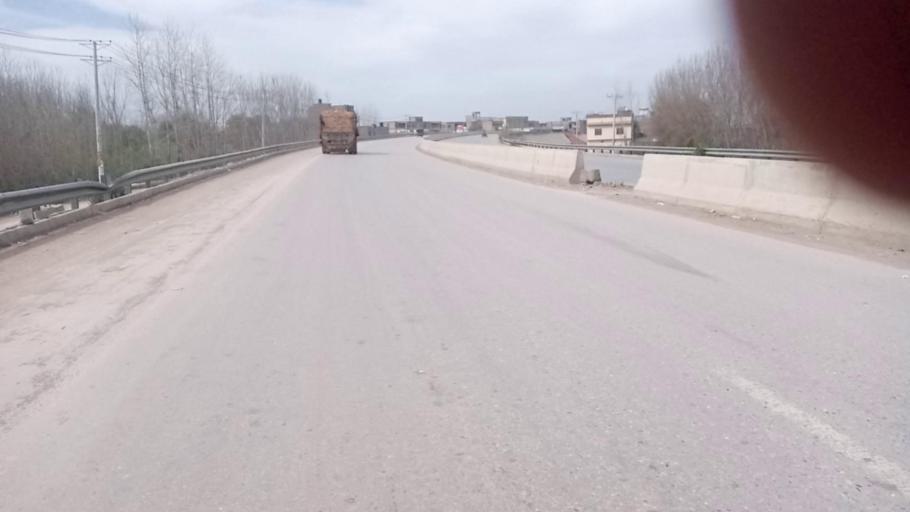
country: PK
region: Khyber Pakhtunkhwa
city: Peshawar
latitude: 34.0283
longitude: 71.6437
